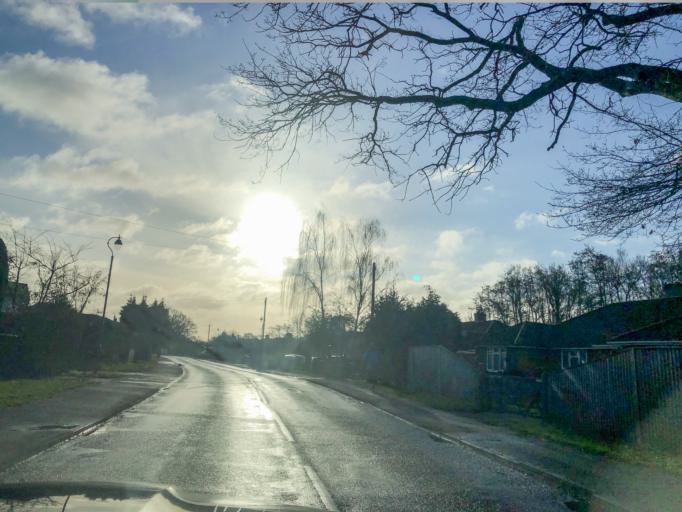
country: GB
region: England
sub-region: Hampshire
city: Farnborough
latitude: 51.2940
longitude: -0.7377
